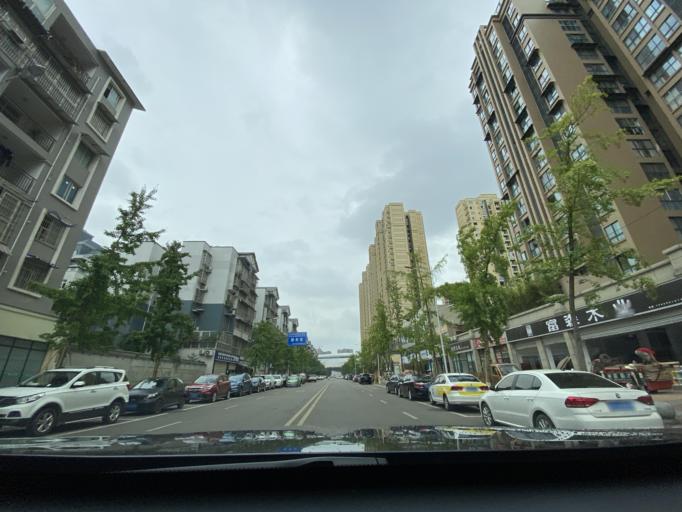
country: CN
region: Sichuan
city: Jiancheng
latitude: 30.4203
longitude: 104.5351
